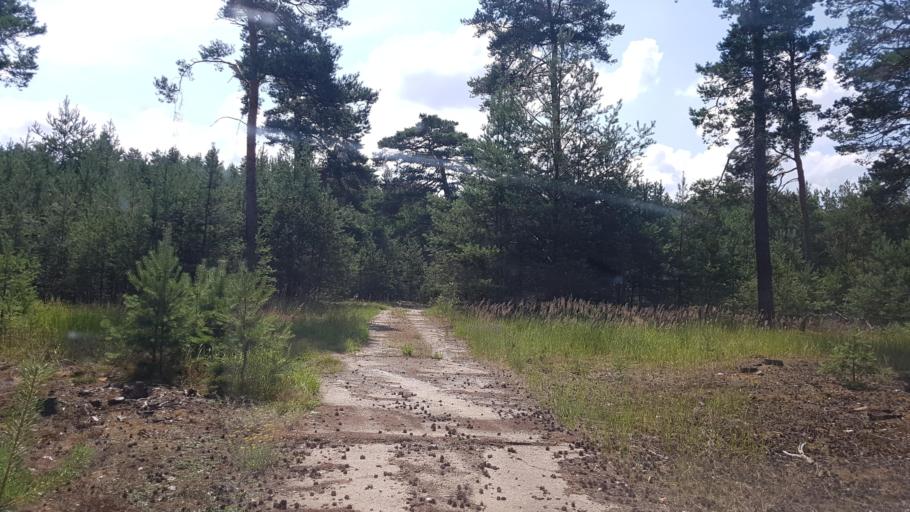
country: DE
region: Brandenburg
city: Crinitz
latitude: 51.7024
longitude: 13.7416
